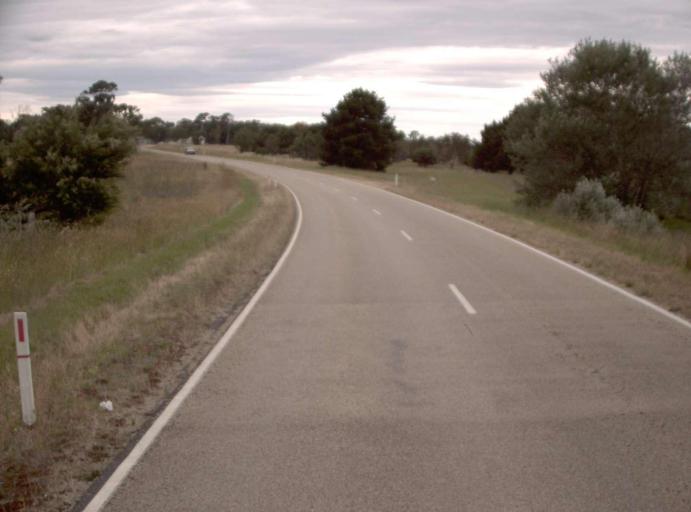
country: AU
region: Victoria
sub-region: East Gippsland
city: Bairnsdale
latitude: -37.9770
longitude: 147.4640
